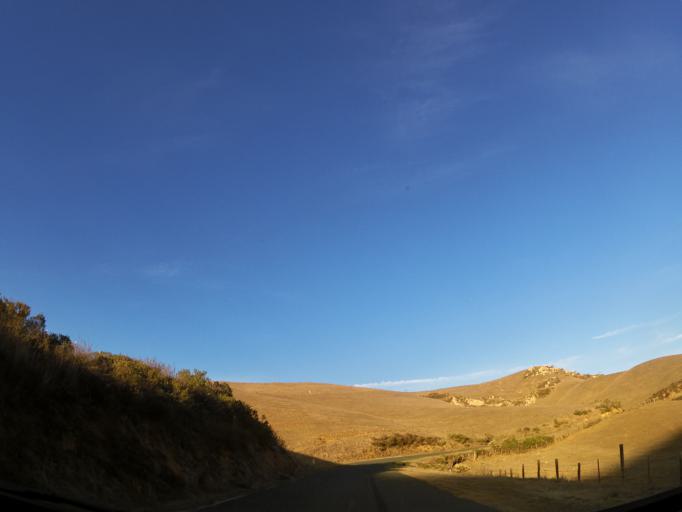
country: US
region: California
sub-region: San Benito County
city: San Juan Bautista
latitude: 36.8116
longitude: -121.5831
